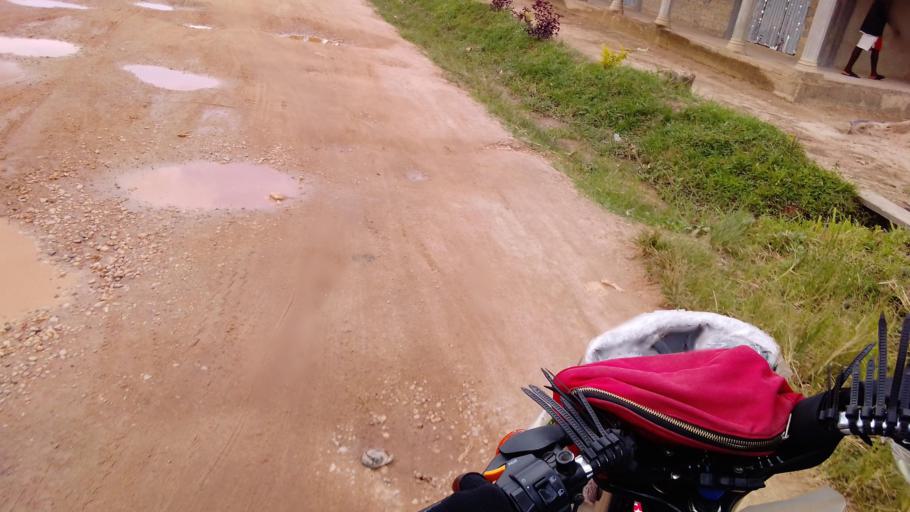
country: SL
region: Eastern Province
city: Koidu
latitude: 8.6735
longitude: -10.9804
